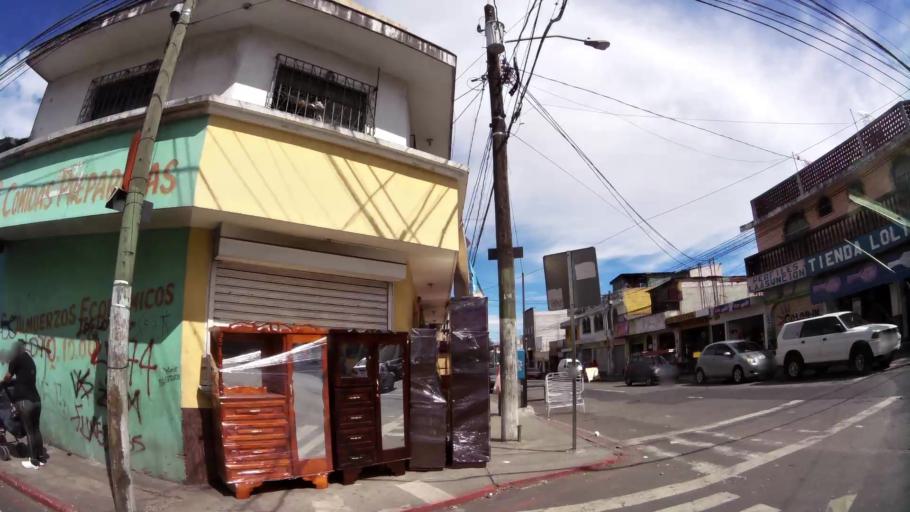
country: GT
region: Guatemala
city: Mixco
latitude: 14.6510
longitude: -90.5828
